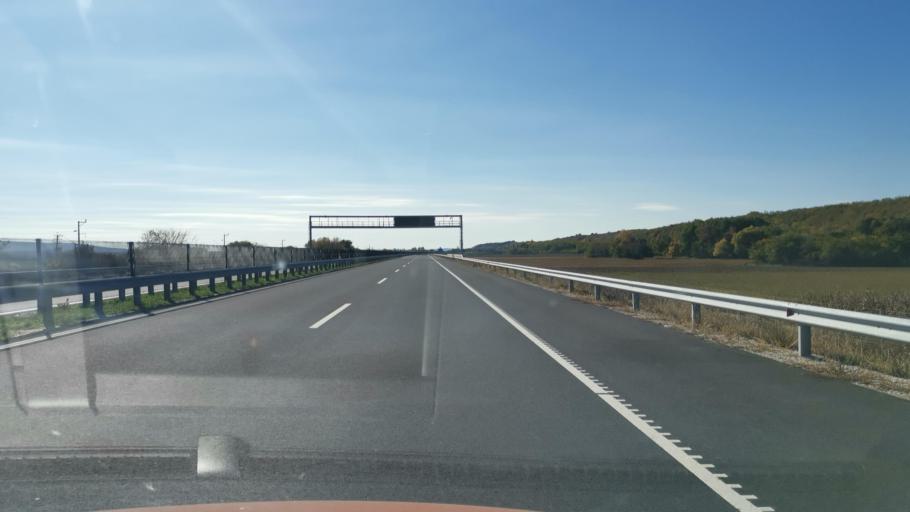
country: HU
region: Borsod-Abauj-Zemplen
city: Gonc
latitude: 48.4392
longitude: 21.1889
